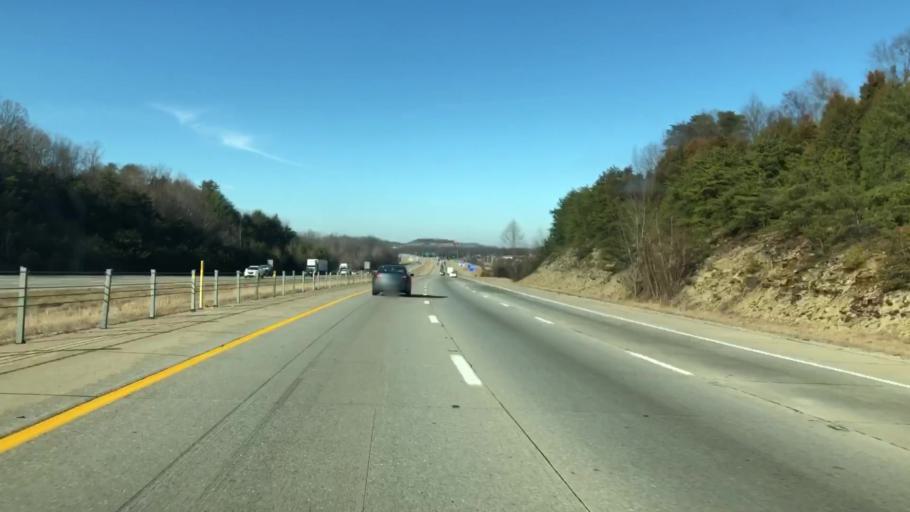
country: US
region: Kentucky
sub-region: Bullitt County
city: Shepherdsville
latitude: 37.9611
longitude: -85.6939
